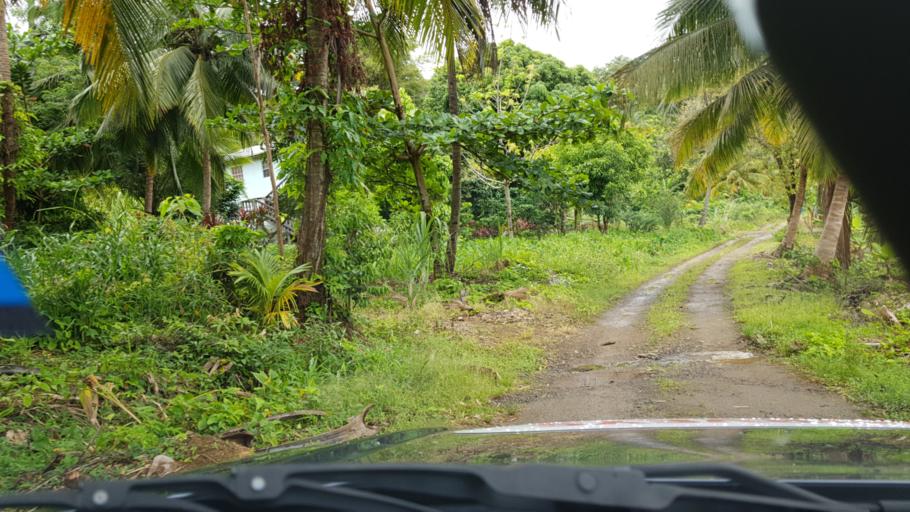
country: LC
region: Anse-la-Raye
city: Anse La Raye
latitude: 13.9453
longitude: -60.9935
